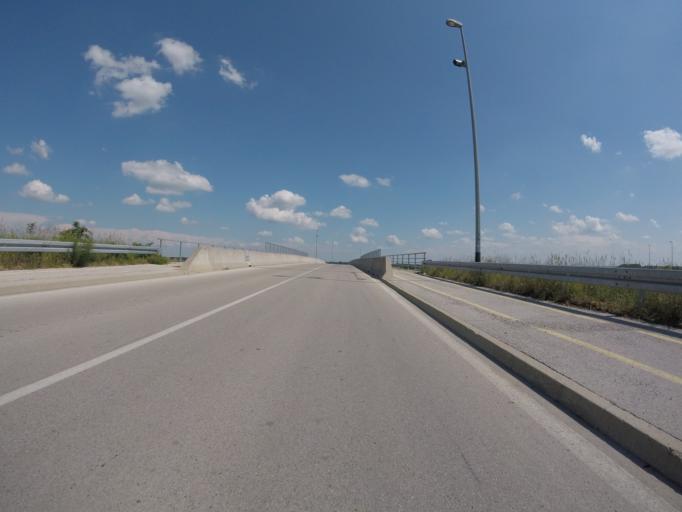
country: HR
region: Zagrebacka
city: Mraclin
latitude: 45.6695
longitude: 16.0770
